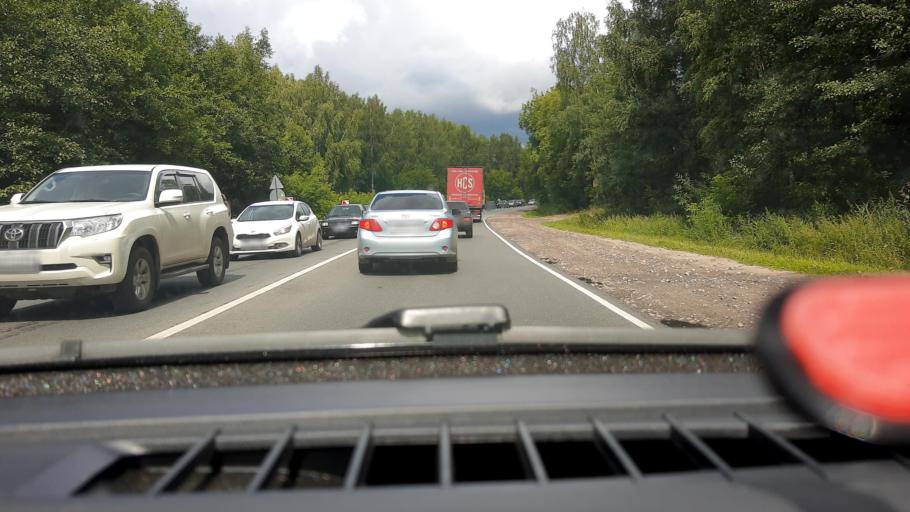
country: RU
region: Nizjnij Novgorod
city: Neklyudovo
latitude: 56.4300
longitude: 43.9900
